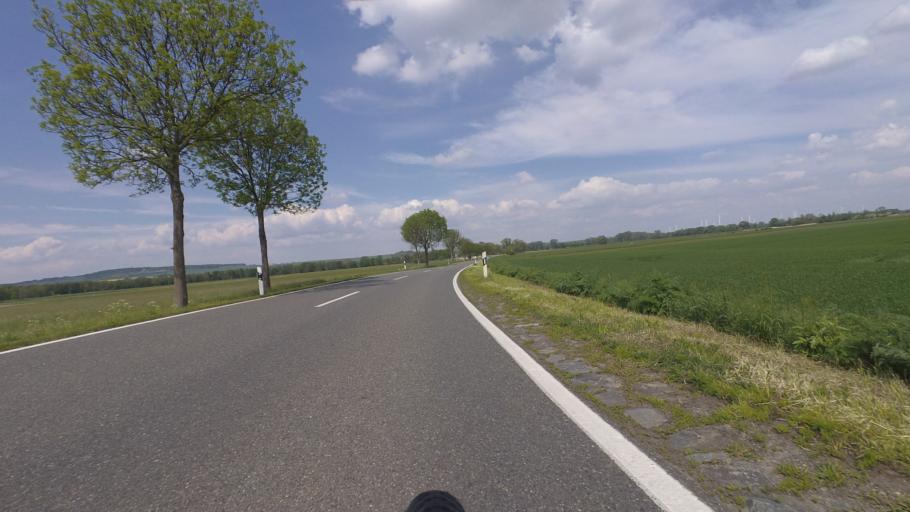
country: DE
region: Lower Saxony
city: Jerxheim
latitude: 52.0538
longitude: 10.8840
